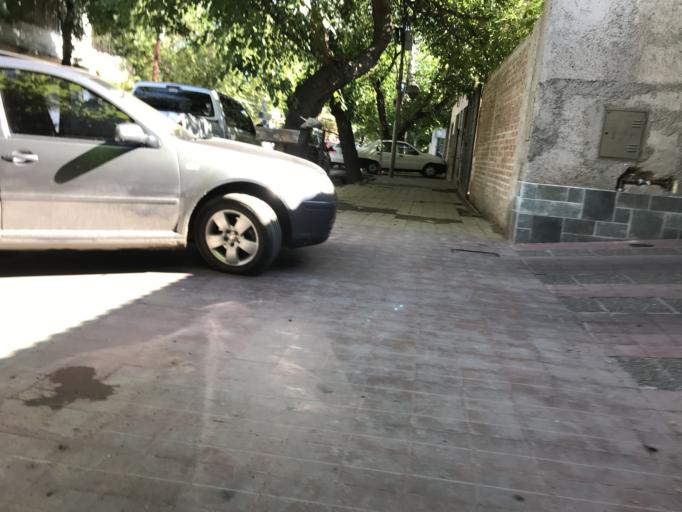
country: AR
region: Mendoza
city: Mendoza
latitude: -32.8819
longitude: -68.8310
